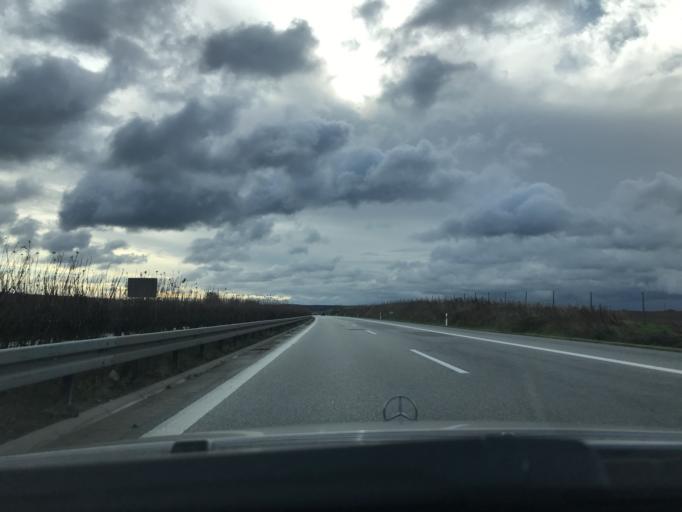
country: DE
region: Mecklenburg-Vorpommern
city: Kessin
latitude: 53.6917
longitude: 13.3260
